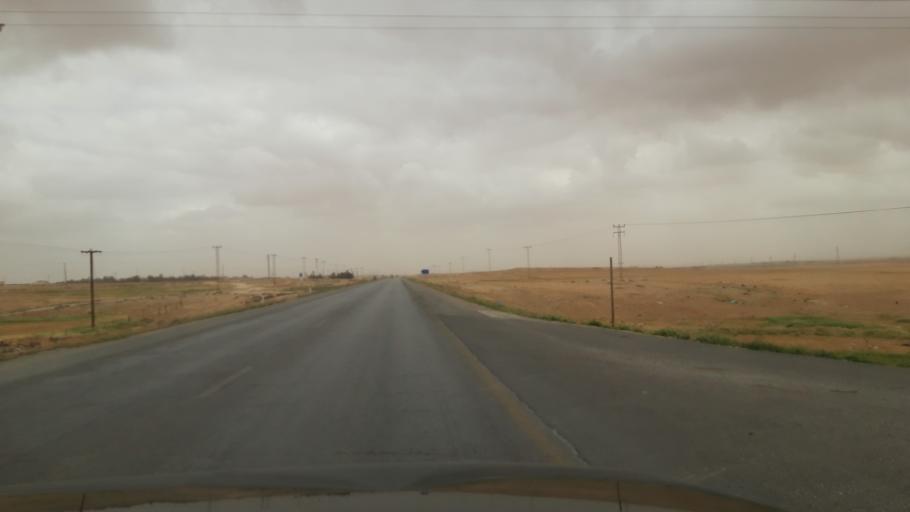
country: JO
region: Amman
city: Sahab
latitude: 31.8010
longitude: 36.1595
